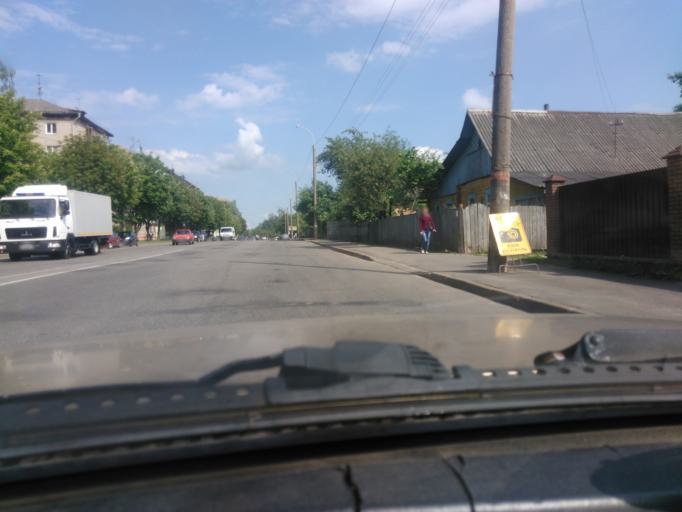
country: BY
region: Mogilev
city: Mahilyow
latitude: 53.9273
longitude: 30.3530
